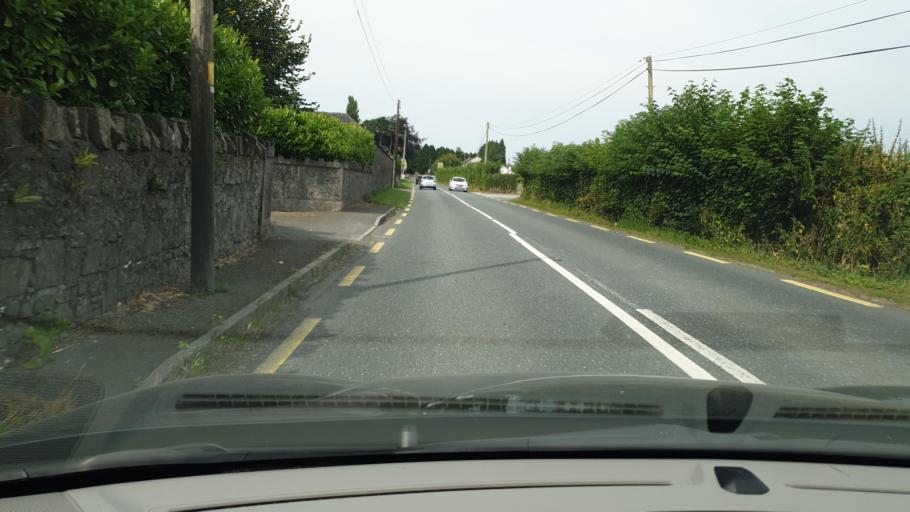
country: IE
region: Leinster
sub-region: An Mhi
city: Athboy
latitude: 53.6459
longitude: -6.8580
